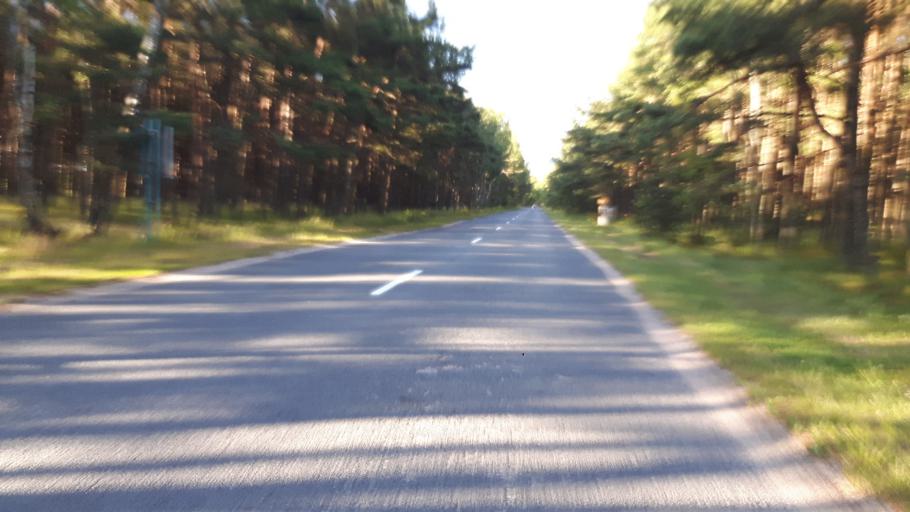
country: LT
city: Nida
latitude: 55.2243
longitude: 20.8941
